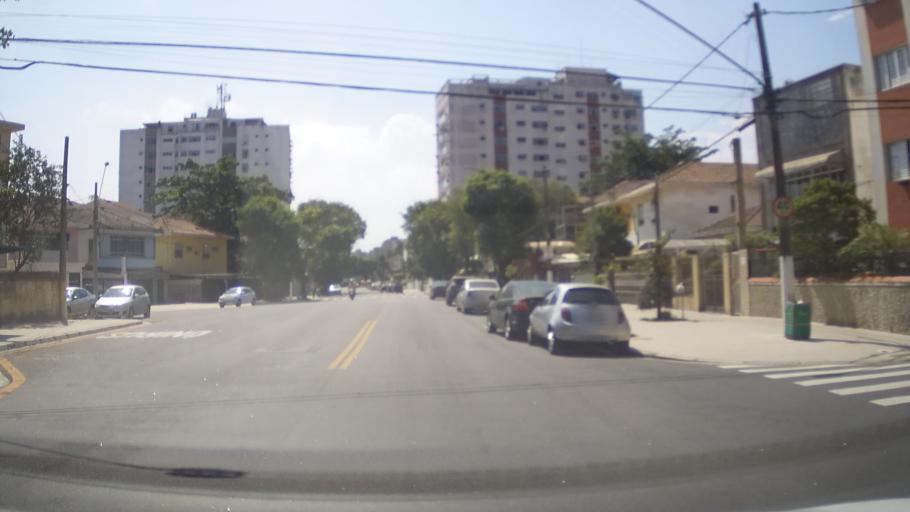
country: BR
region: Sao Paulo
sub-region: Santos
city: Santos
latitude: -23.9841
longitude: -46.2981
